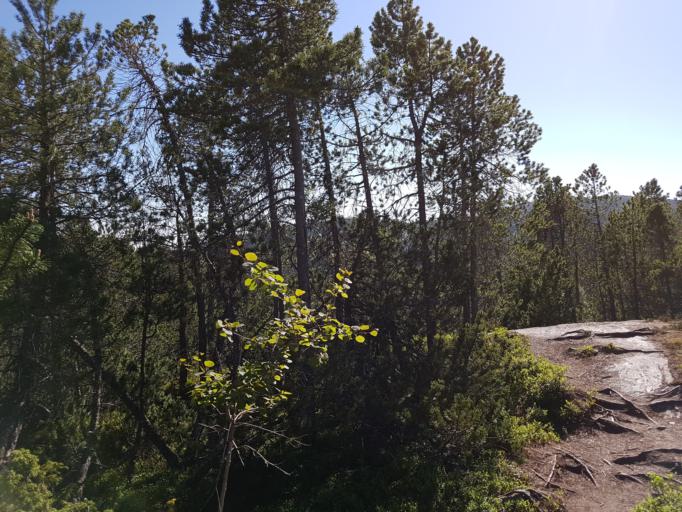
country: NO
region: Sor-Trondelag
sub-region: Trondheim
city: Trondheim
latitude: 63.4293
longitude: 10.2900
